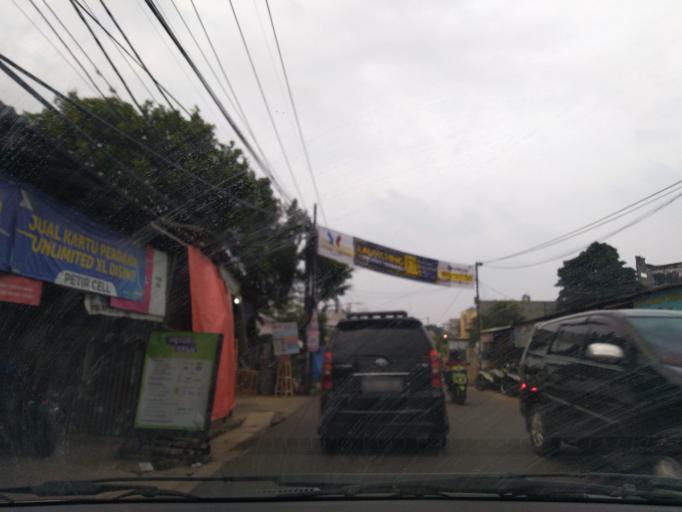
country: ID
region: Banten
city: South Tangerang
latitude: -6.2617
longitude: 106.7462
